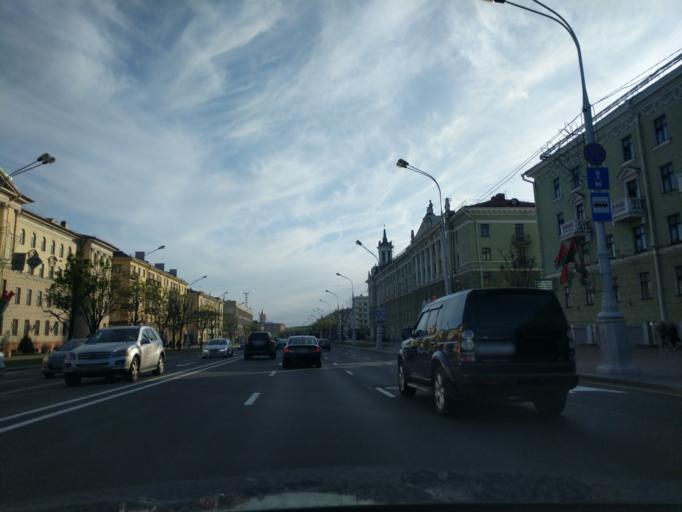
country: BY
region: Minsk
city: Minsk
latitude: 53.9198
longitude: 27.5930
